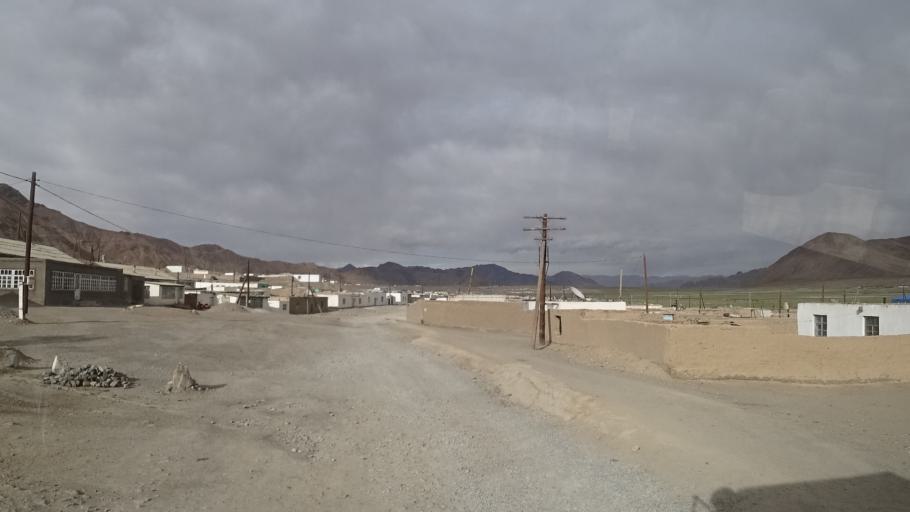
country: TJ
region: Gorno-Badakhshan
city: Murghob
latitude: 38.1736
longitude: 73.9690
